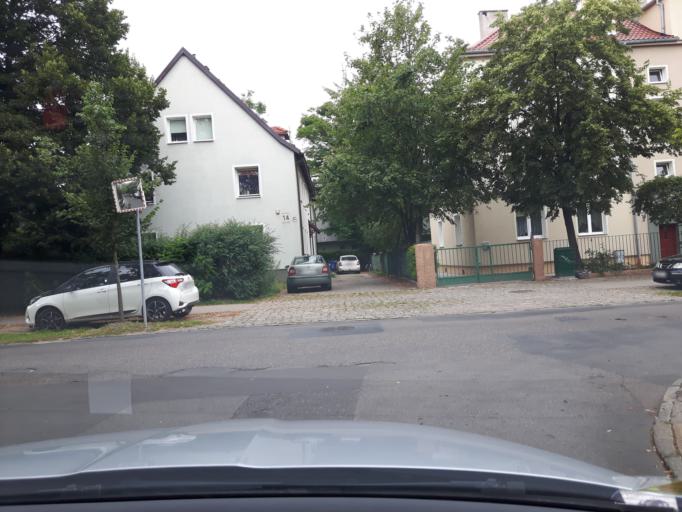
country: PL
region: Pomeranian Voivodeship
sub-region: Sopot
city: Sopot
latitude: 54.4331
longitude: 18.5679
